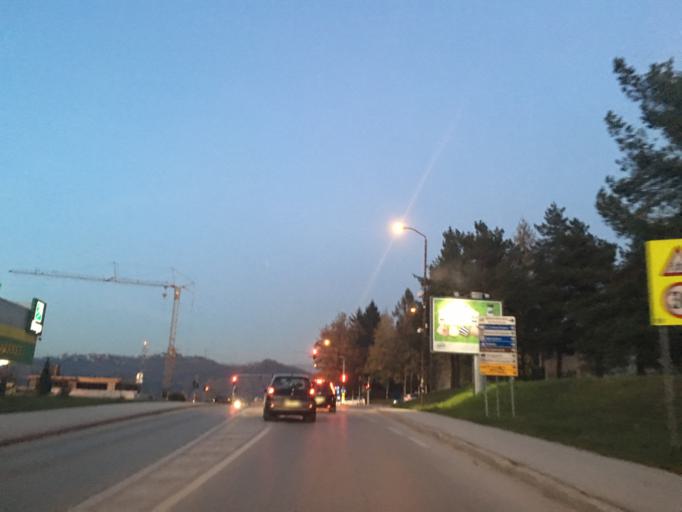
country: BA
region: Federation of Bosnia and Herzegovina
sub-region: Kanton Sarajevo
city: Sarajevo
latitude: 43.8234
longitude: 18.3624
